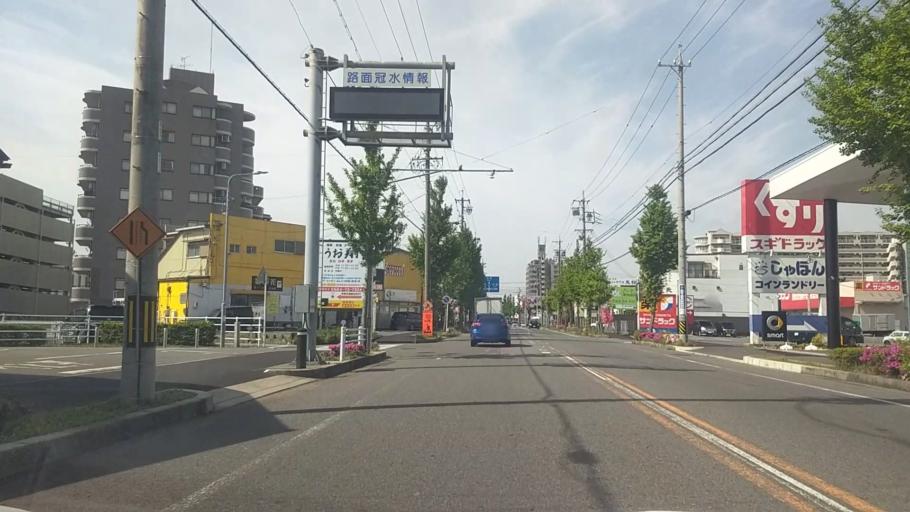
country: JP
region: Aichi
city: Okazaki
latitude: 34.9357
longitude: 137.1468
